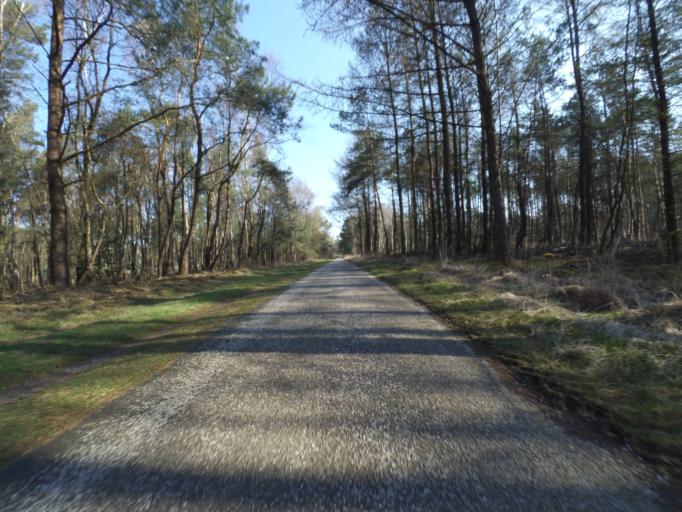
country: NL
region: Gelderland
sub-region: Gemeente Arnhem
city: Hoogkamp
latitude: 52.0498
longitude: 5.8536
